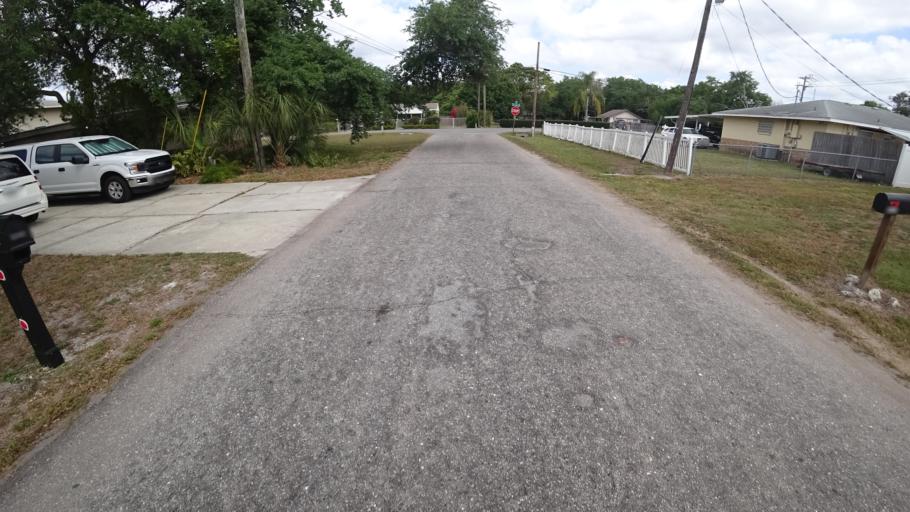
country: US
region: Florida
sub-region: Manatee County
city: South Bradenton
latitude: 27.4437
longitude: -82.5820
